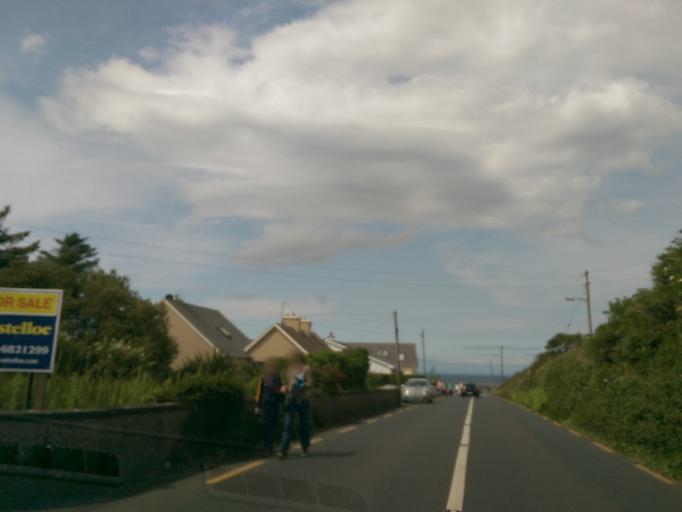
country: IE
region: Munster
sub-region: An Clar
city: Kilrush
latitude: 52.8097
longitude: -9.4539
